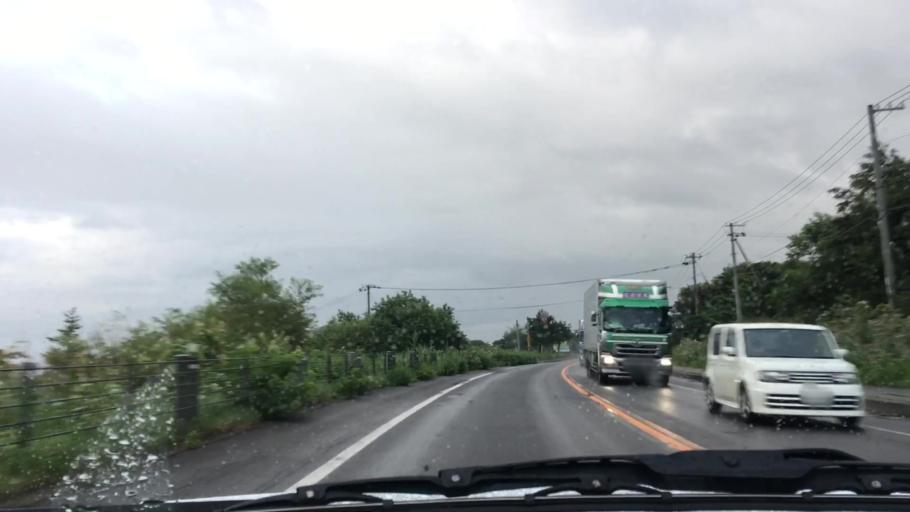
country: JP
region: Hokkaido
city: Nanae
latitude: 42.1783
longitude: 140.4465
